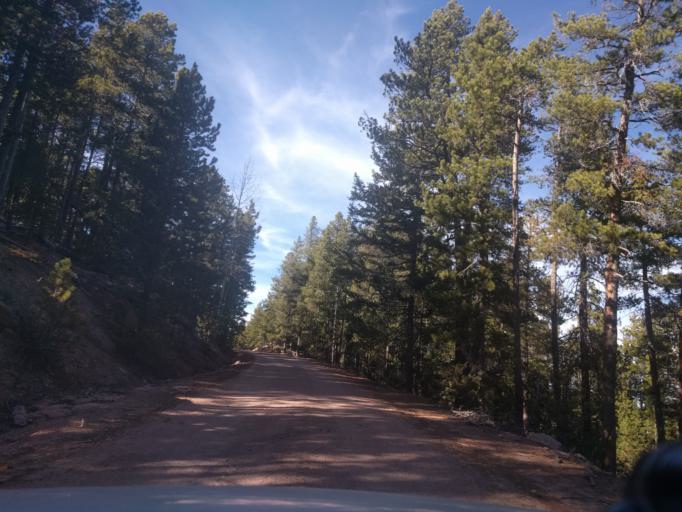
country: US
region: Colorado
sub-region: Douglas County
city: Perry Park
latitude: 39.2046
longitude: -105.0522
